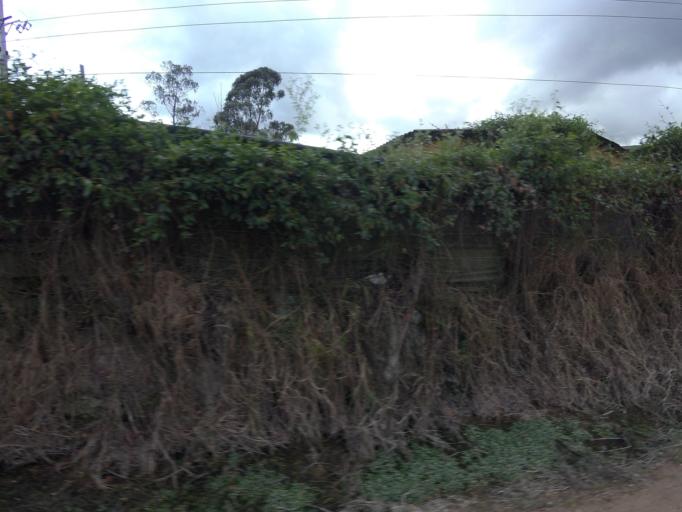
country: CO
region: Cundinamarca
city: Tabio
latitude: 4.9340
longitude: -74.0903
